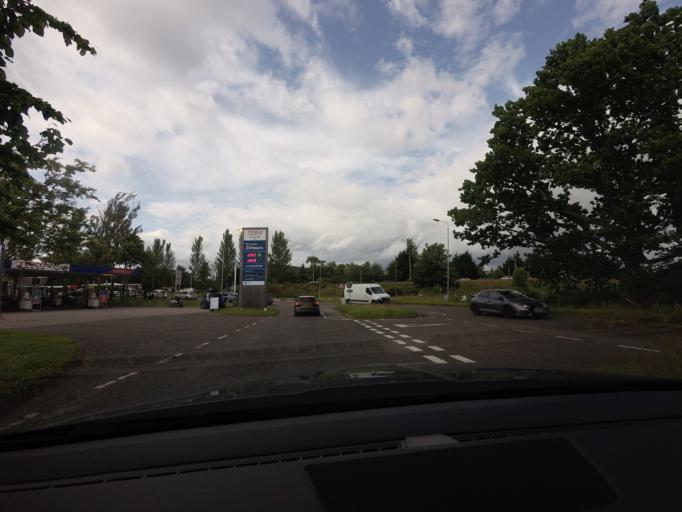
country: GB
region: Scotland
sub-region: Highland
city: Inverness
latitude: 57.4710
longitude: -4.1877
